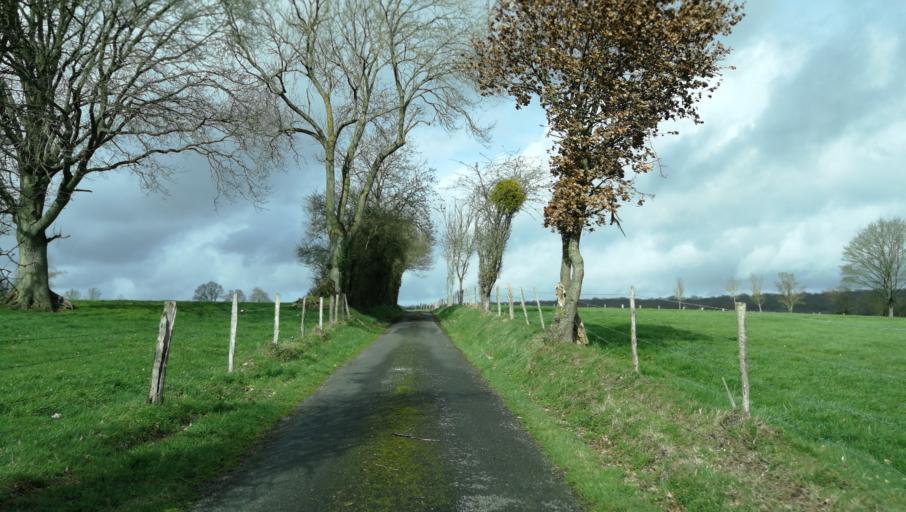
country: FR
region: Haute-Normandie
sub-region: Departement de l'Eure
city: Lieurey
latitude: 49.2304
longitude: 0.5413
